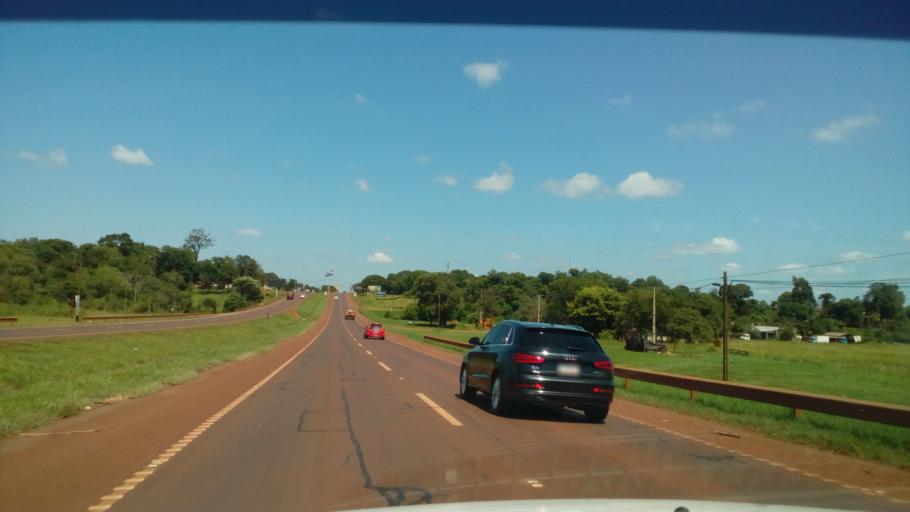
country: PY
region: Alto Parana
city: Colonia Yguazu
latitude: -25.4850
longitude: -54.8901
